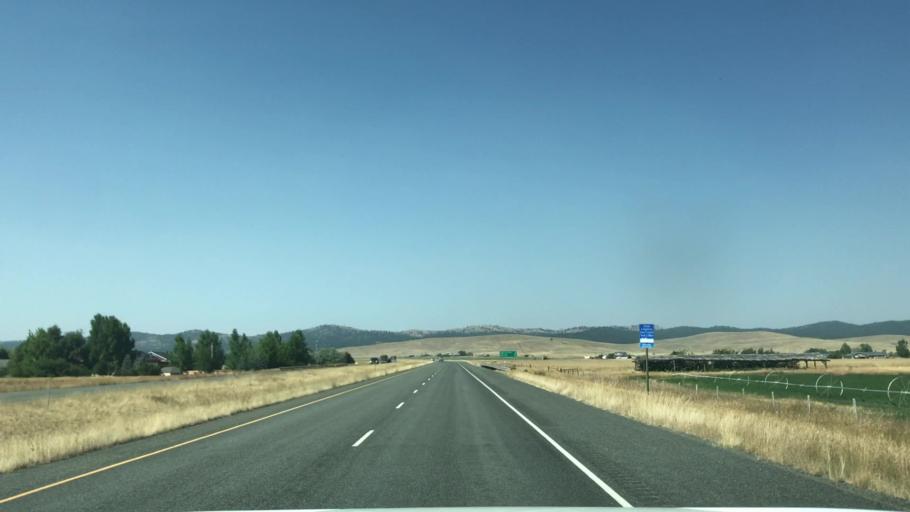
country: US
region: Montana
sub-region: Lewis and Clark County
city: Helena Valley Northwest
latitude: 46.7138
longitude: -112.0120
